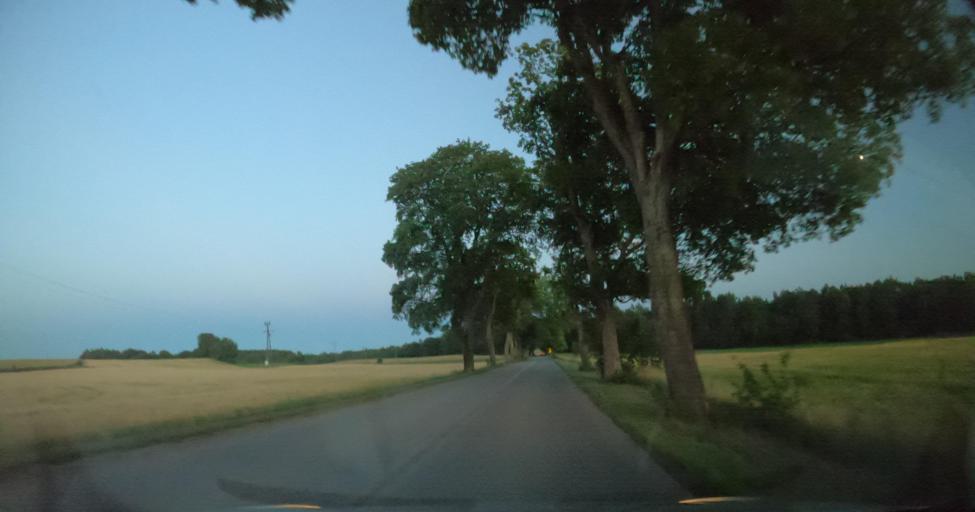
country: PL
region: Pomeranian Voivodeship
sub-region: Powiat wejherowski
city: Szemud
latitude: 54.4699
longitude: 18.2799
